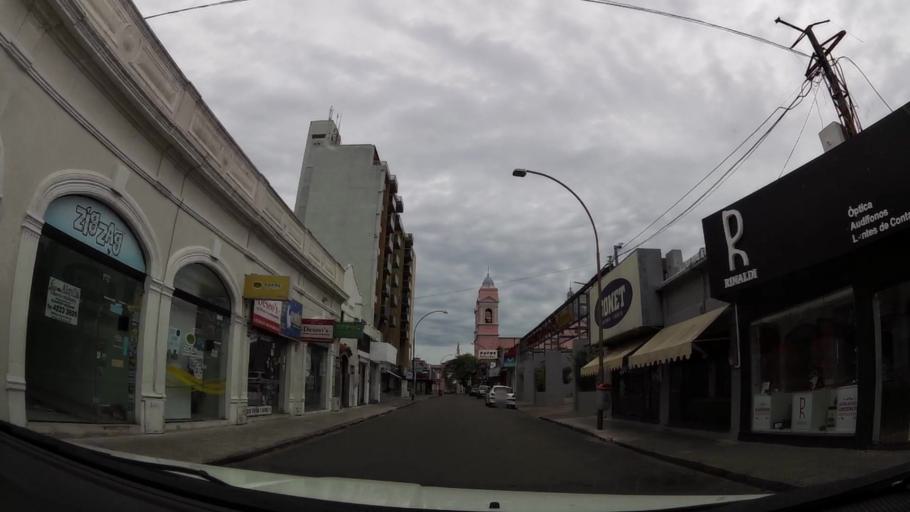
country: UY
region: Maldonado
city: Maldonado
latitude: -34.9076
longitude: -54.9588
